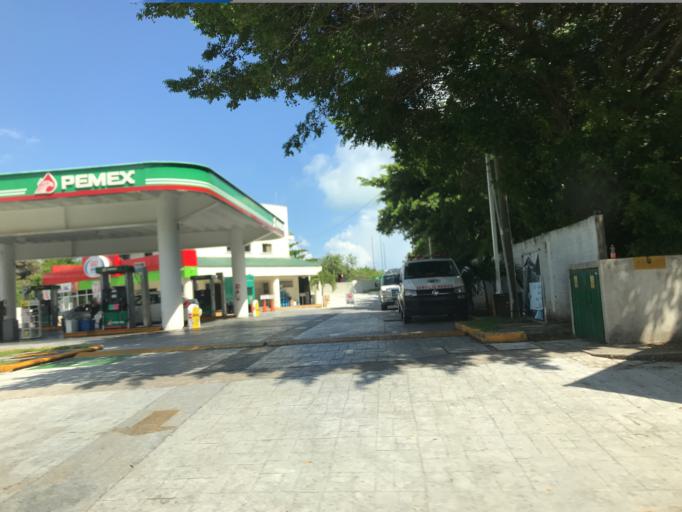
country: MX
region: Quintana Roo
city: Cancun
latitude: 21.1547
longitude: -86.8213
